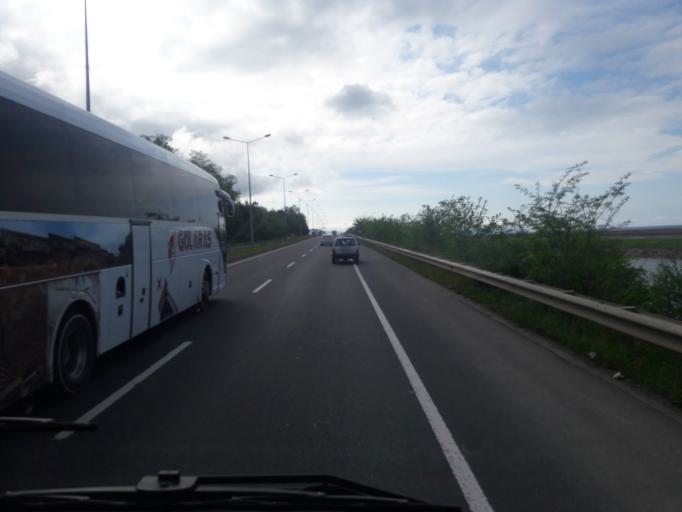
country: TR
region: Giresun
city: Piraziz
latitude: 40.9617
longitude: 38.1017
